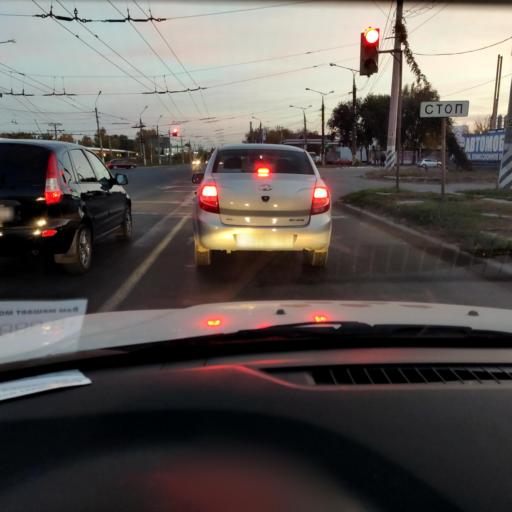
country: RU
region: Samara
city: Tol'yatti
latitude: 53.5323
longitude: 49.4389
